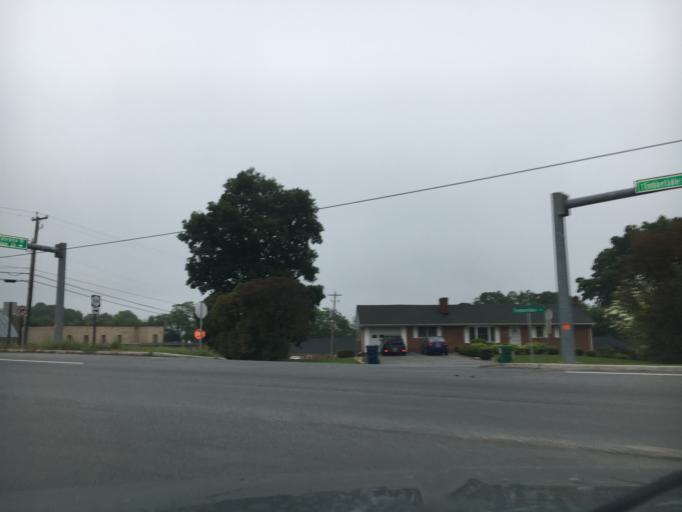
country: US
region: Virginia
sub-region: Campbell County
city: Timberlake
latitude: 37.3421
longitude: -79.2363
